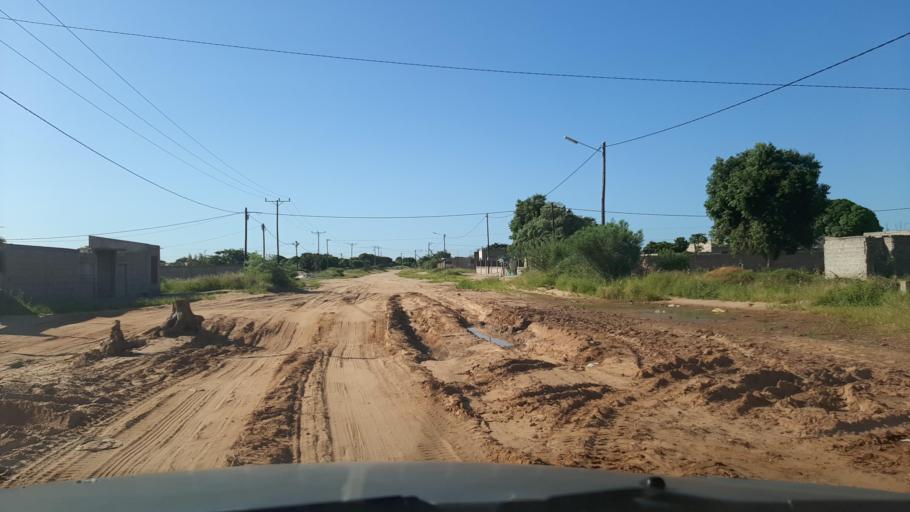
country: MZ
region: Maputo City
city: Maputo
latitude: -25.7672
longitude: 32.5478
